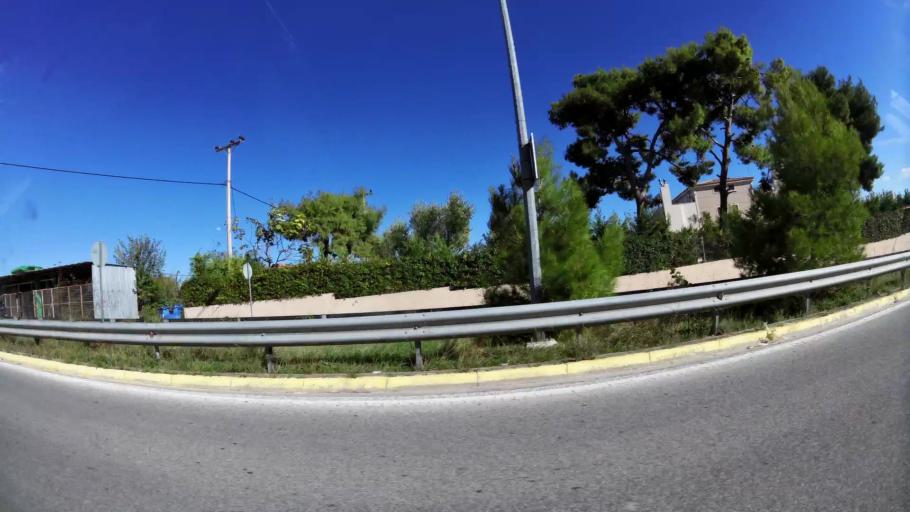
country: GR
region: Attica
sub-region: Nomarchia Anatolikis Attikis
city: Pallini
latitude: 38.0033
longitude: 23.8924
